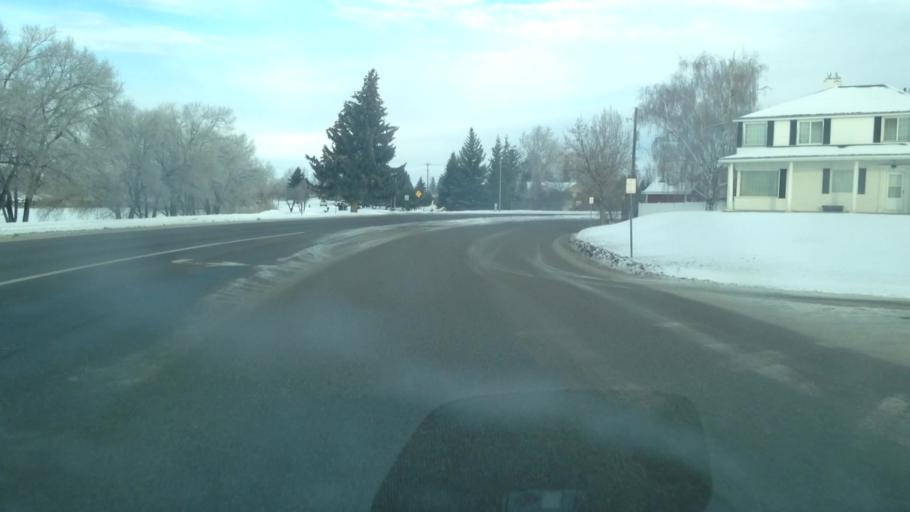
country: US
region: Idaho
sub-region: Bonneville County
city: Idaho Falls
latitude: 43.5044
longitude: -112.0461
